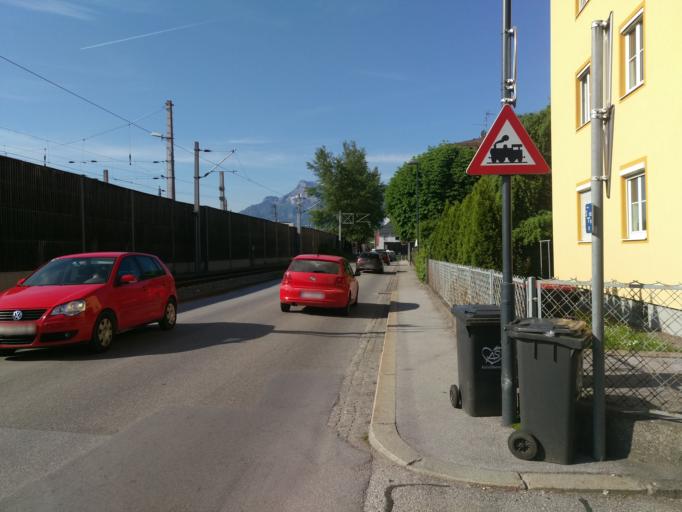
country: AT
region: Salzburg
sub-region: Politischer Bezirk Salzburg-Umgebung
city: Bergheim
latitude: 47.8197
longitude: 13.0480
